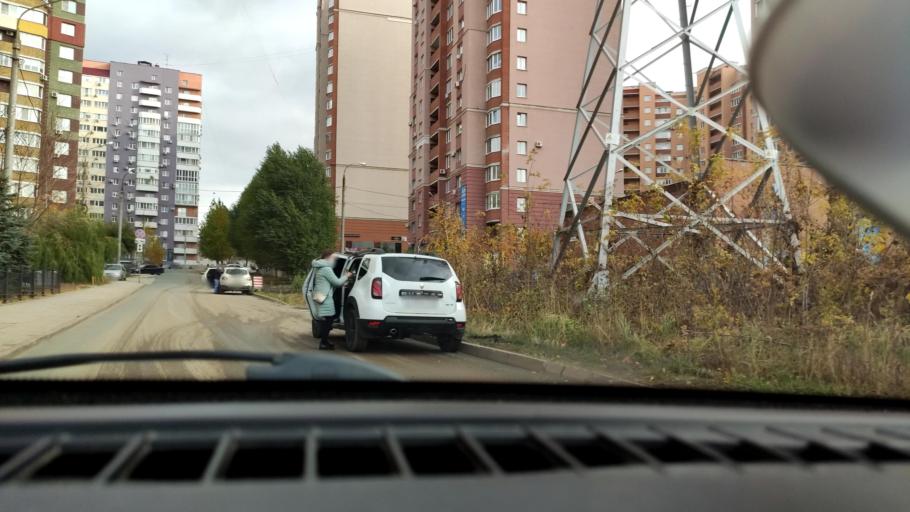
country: RU
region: Samara
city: Samara
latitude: 53.2466
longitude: 50.1883
